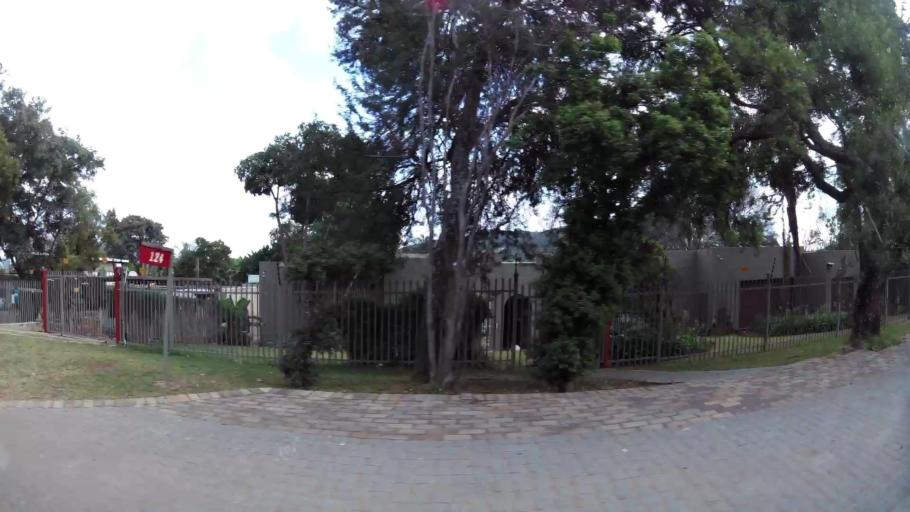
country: ZA
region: Gauteng
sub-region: City of Tshwane Metropolitan Municipality
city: Pretoria
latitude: -25.7587
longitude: 28.2934
